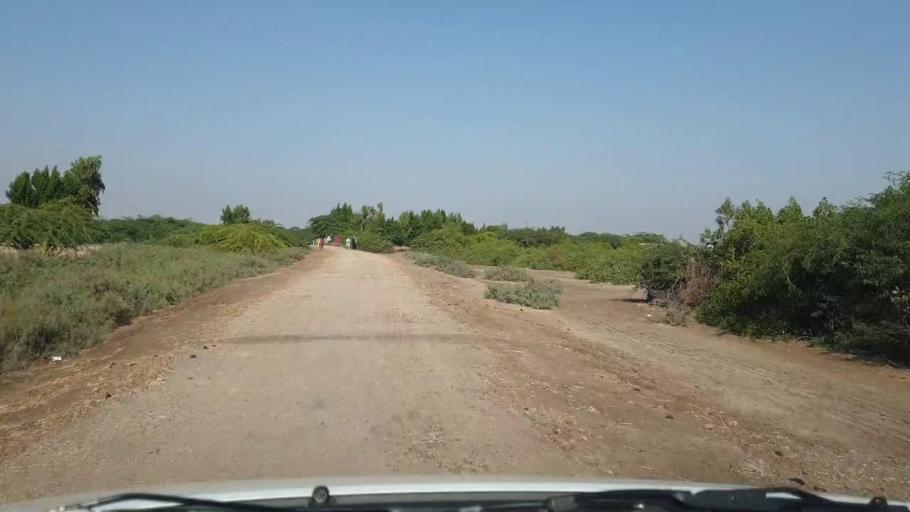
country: PK
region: Sindh
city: Mirpur Sakro
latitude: 24.6484
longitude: 67.6361
